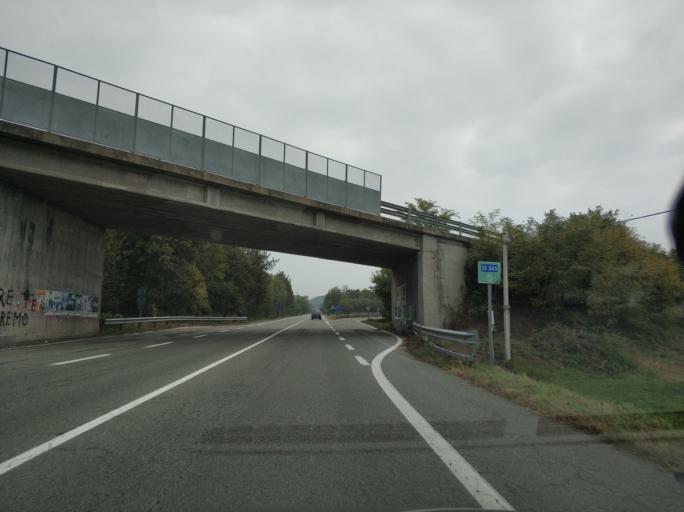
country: IT
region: Piedmont
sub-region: Provincia di Torino
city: Bairo
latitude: 45.3859
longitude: 7.7372
